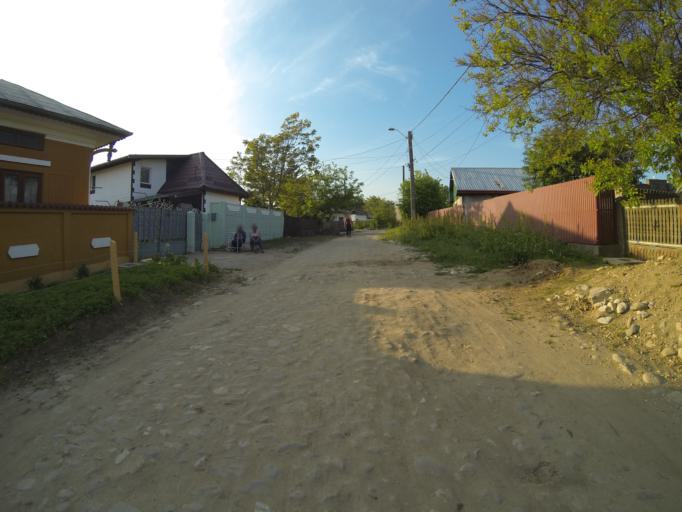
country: RO
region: Dolj
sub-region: Comuna Segarcea
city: Segarcea
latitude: 44.0982
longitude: 23.7456
